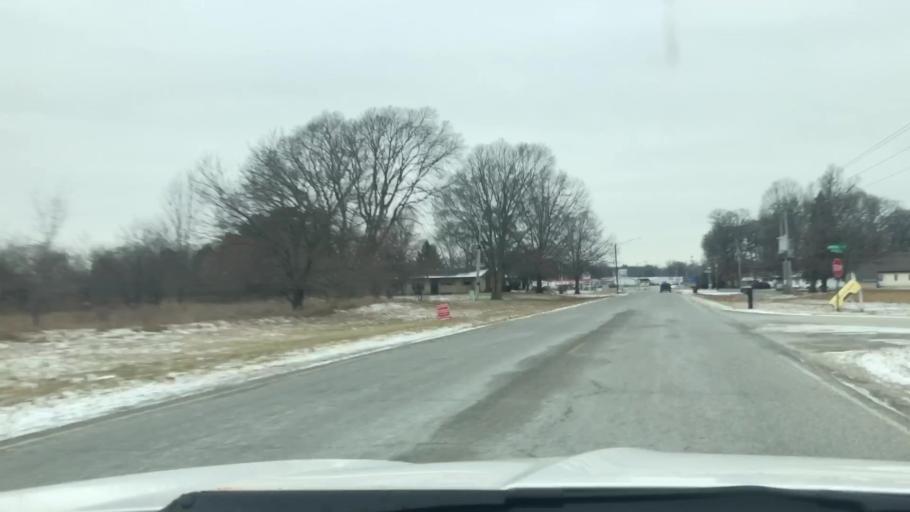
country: US
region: Indiana
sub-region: Fulton County
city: Rochester
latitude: 41.0520
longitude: -86.2126
